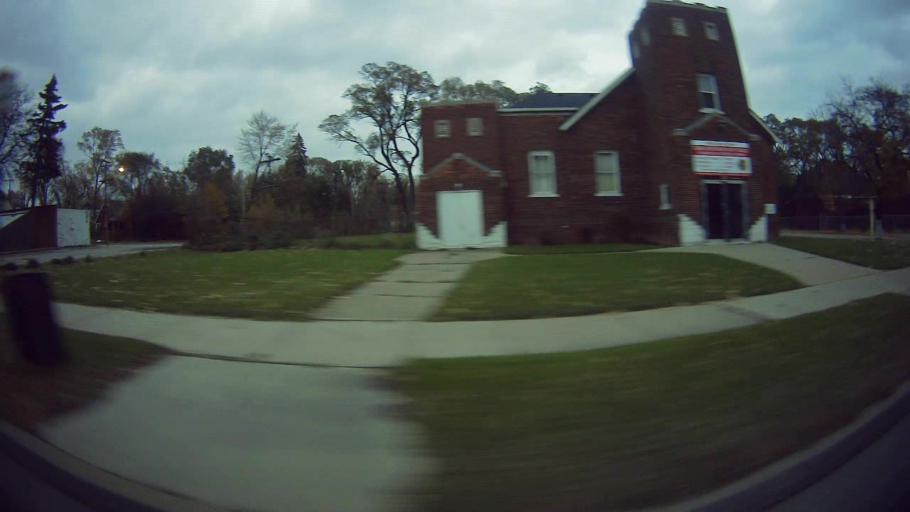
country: US
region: Michigan
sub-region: Wayne County
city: Hamtramck
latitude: 42.4026
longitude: -82.9945
